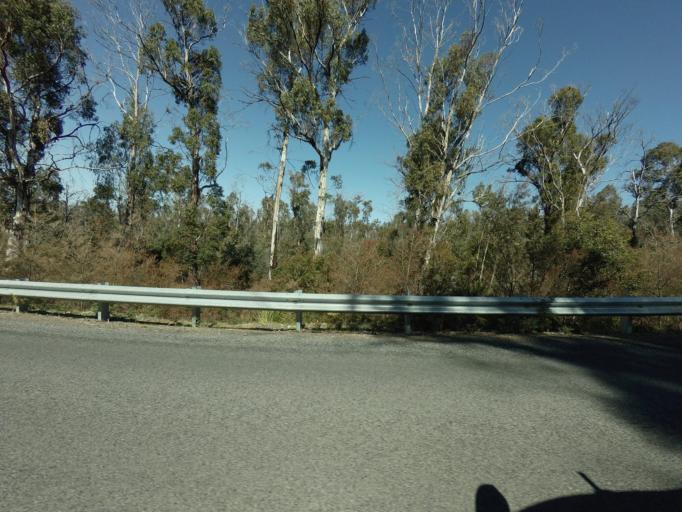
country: AU
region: Tasmania
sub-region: Derwent Valley
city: New Norfolk
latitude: -42.5458
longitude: 146.7149
